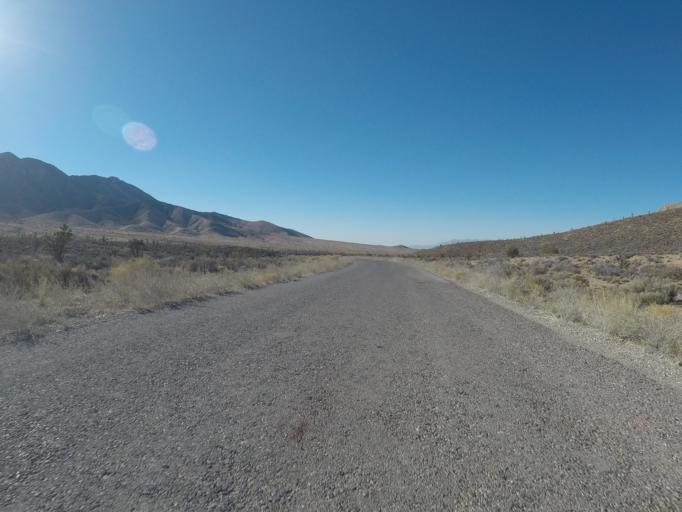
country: US
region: Nevada
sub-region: Clark County
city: Sandy Valley
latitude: 36.0226
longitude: -115.5608
